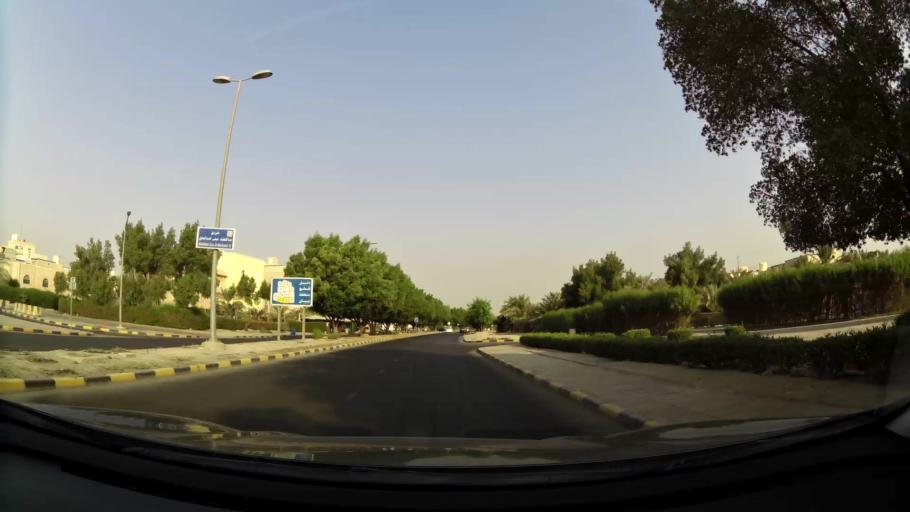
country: KW
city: Bayan
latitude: 29.2877
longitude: 48.0579
